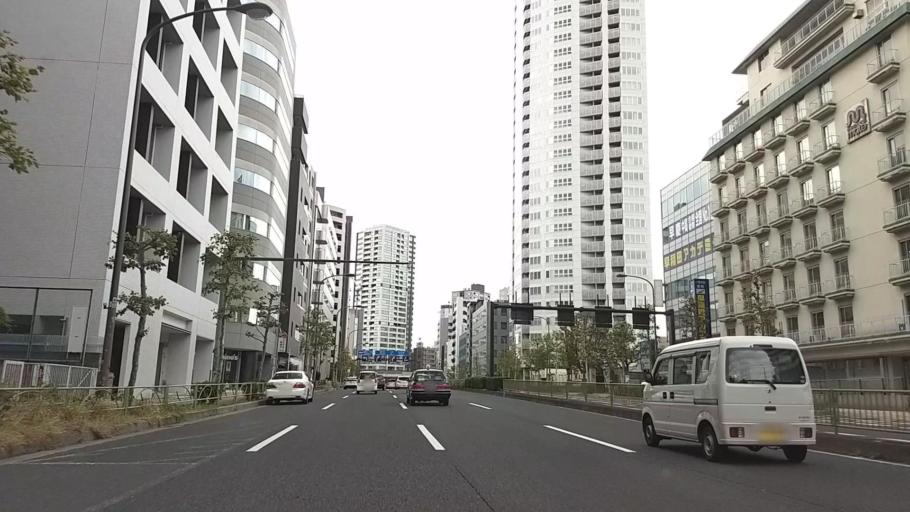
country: JP
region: Tokyo
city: Tokyo
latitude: 35.6355
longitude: 139.7314
